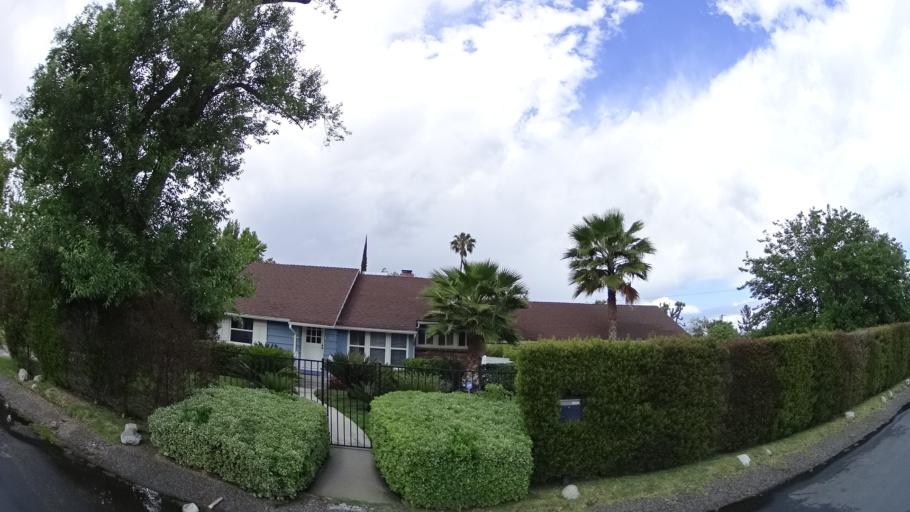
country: US
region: California
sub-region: Los Angeles County
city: North Hollywood
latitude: 34.1550
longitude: -118.4033
